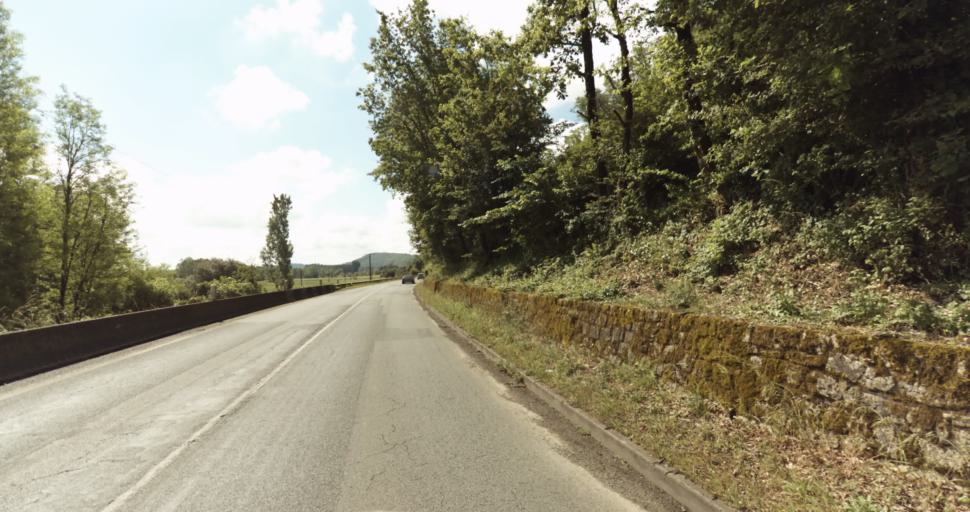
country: FR
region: Aquitaine
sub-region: Departement de la Dordogne
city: Le Bugue
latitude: 44.8401
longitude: 0.9325
